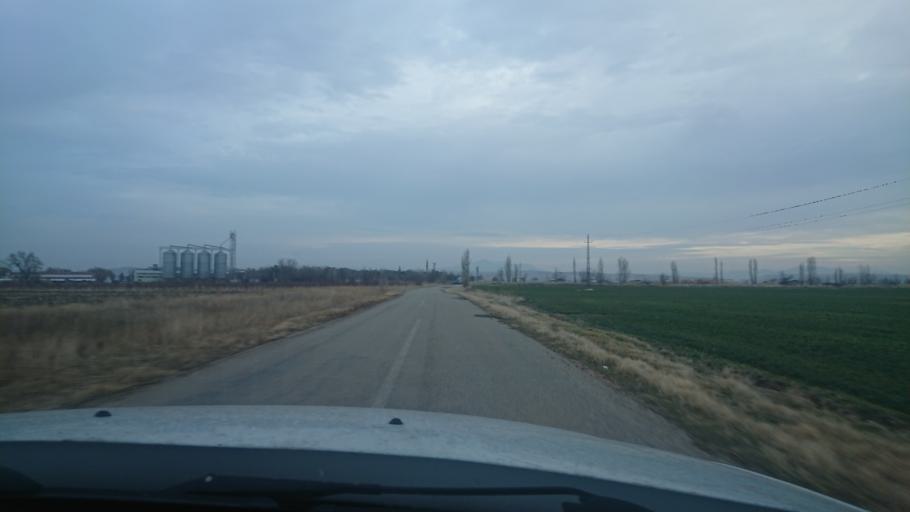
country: TR
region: Aksaray
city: Yesilova
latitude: 38.4525
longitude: 33.8360
